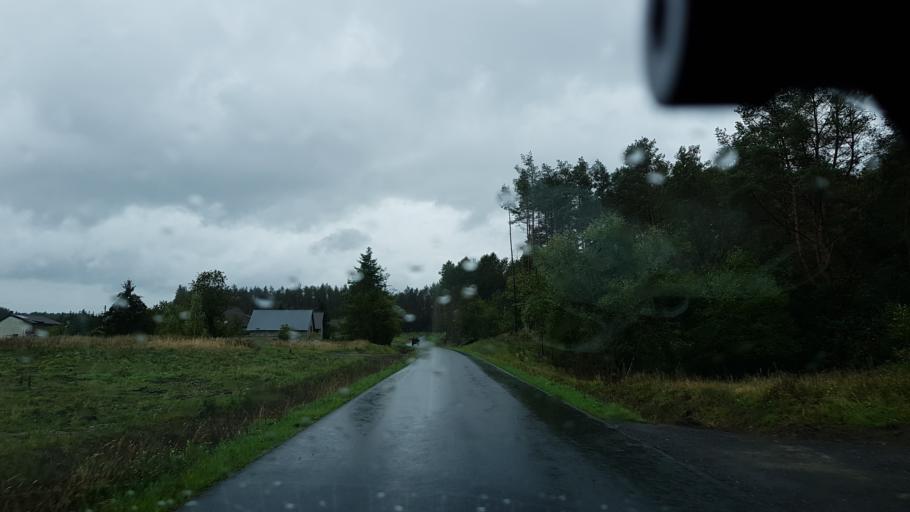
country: PL
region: West Pomeranian Voivodeship
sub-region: Powiat goleniowski
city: Przybiernow
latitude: 53.7417
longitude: 14.7735
